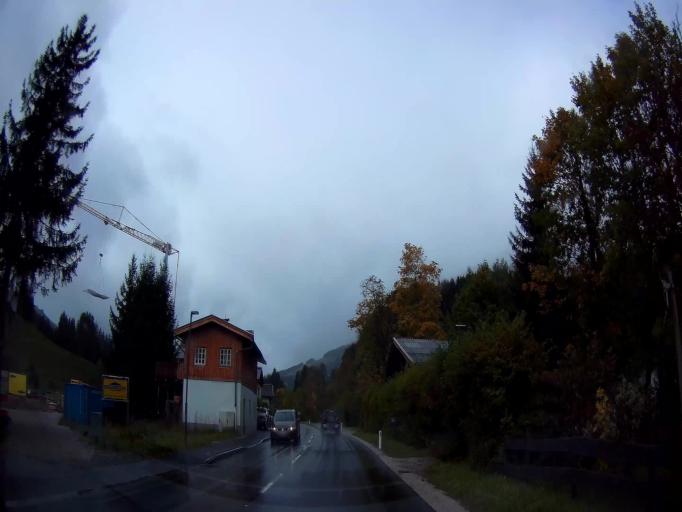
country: AT
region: Salzburg
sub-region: Politischer Bezirk Zell am See
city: Leogang
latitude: 47.4392
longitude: 12.7524
